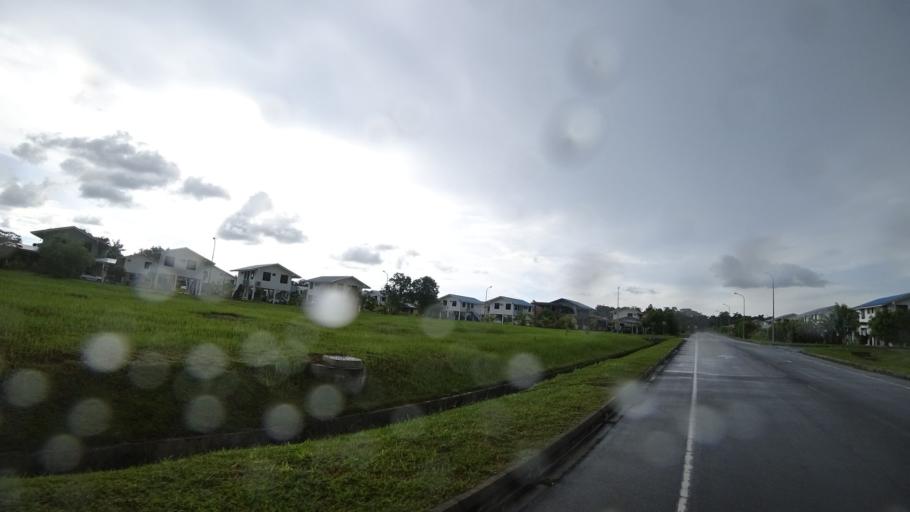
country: BN
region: Brunei and Muara
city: Bandar Seri Begawan
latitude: 4.8368
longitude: 114.9126
